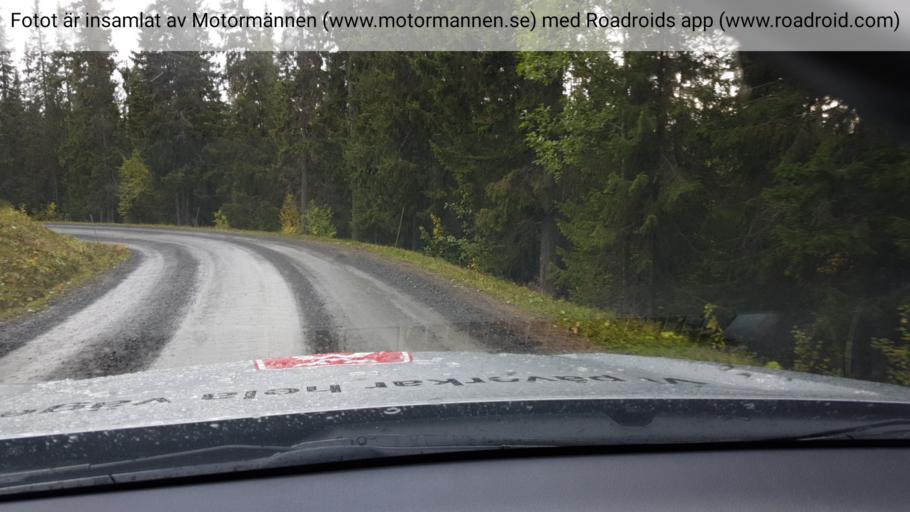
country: NO
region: Nord-Trondelag
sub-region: Lierne
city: Sandvika
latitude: 64.1106
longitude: 14.1478
